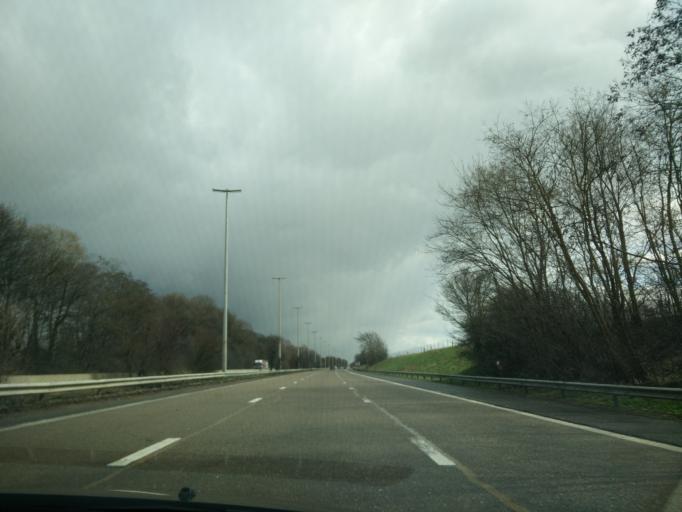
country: BE
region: Wallonia
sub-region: Province de Liege
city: Oreye
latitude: 50.7011
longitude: 5.3509
